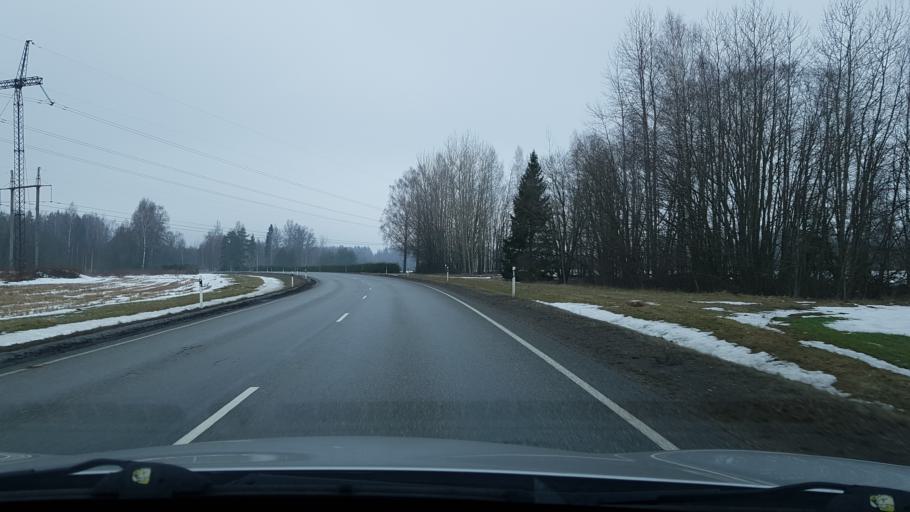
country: EE
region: Valgamaa
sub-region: Valga linn
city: Valga
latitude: 57.9465
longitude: 26.1689
